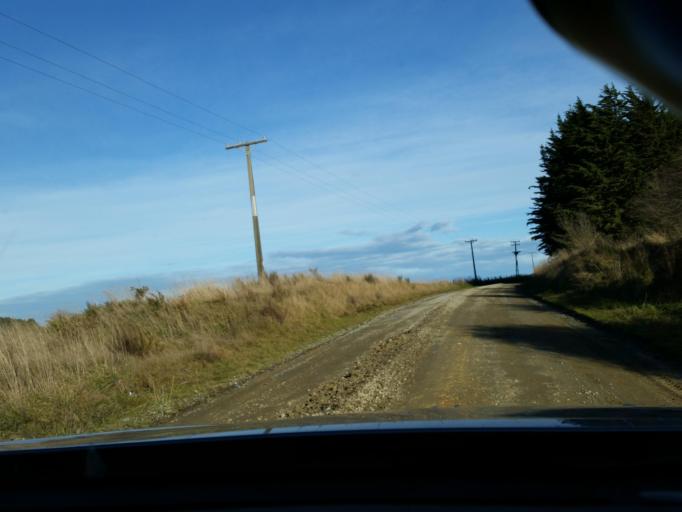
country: NZ
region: Southland
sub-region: Southland District
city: Winton
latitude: -46.2470
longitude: 168.4713
